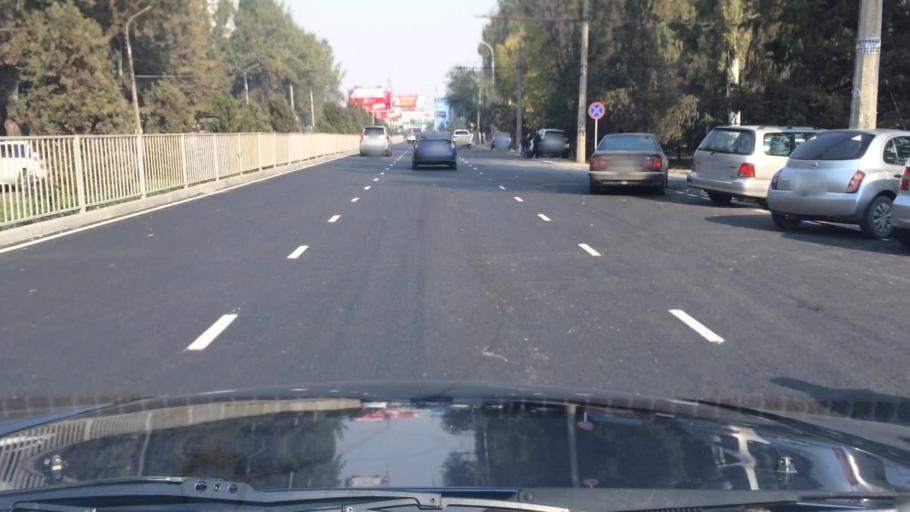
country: KG
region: Chuy
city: Lebedinovka
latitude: 42.8729
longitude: 74.6371
